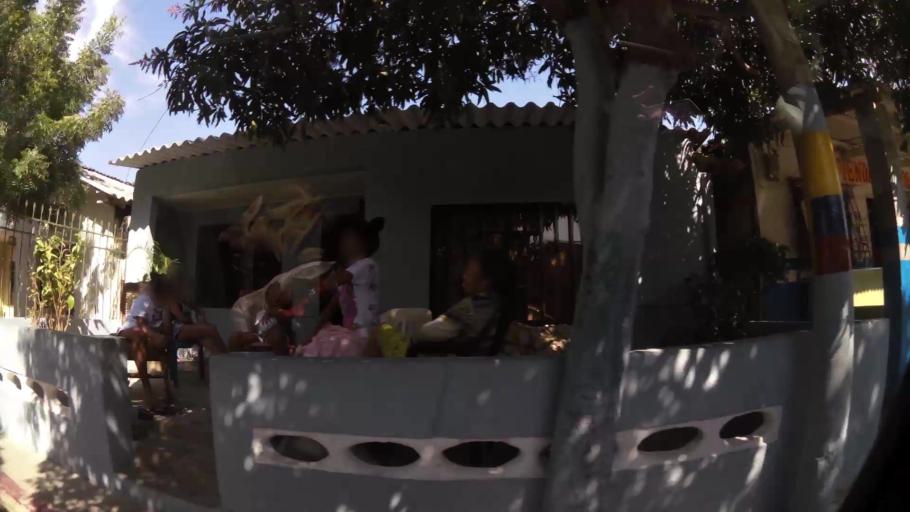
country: CO
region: Atlantico
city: Barranquilla
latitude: 10.9310
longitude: -74.8257
